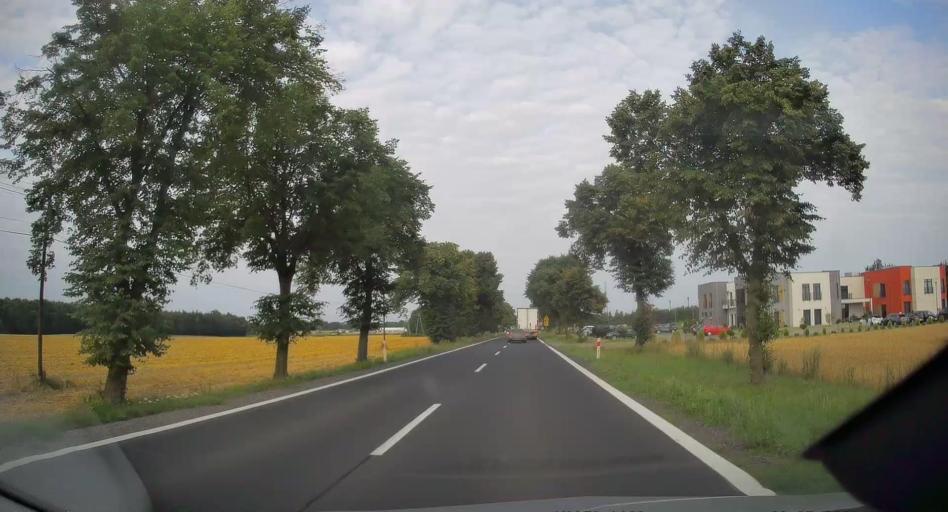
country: PL
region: Silesian Voivodeship
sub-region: Powiat czestochowski
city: Klomnice
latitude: 50.9161
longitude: 19.3296
